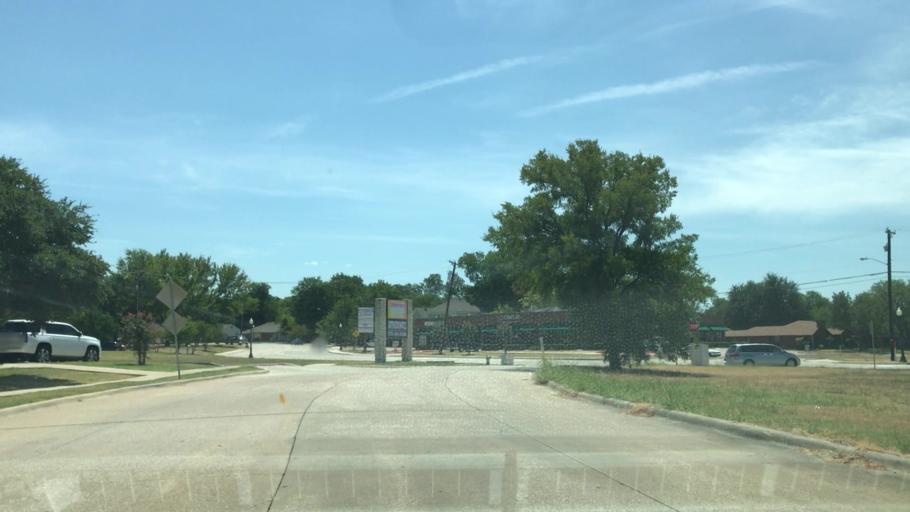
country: US
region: Texas
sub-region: Collin County
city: Wylie
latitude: 33.0187
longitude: -96.5444
